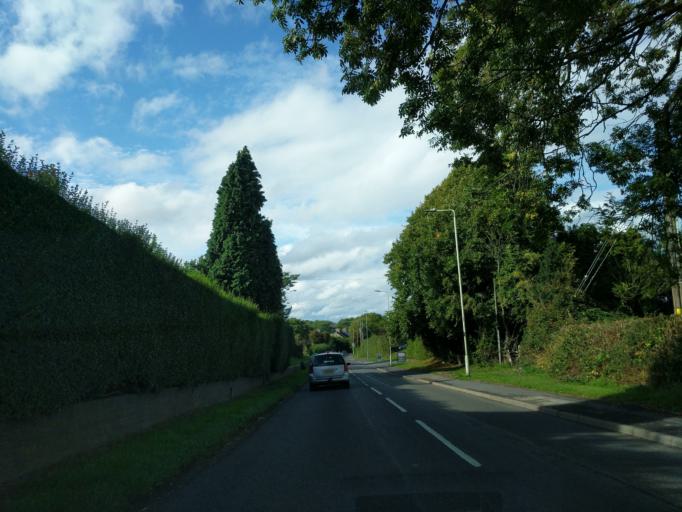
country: GB
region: England
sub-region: Leicestershire
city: Coalville
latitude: 52.7039
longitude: -1.3716
